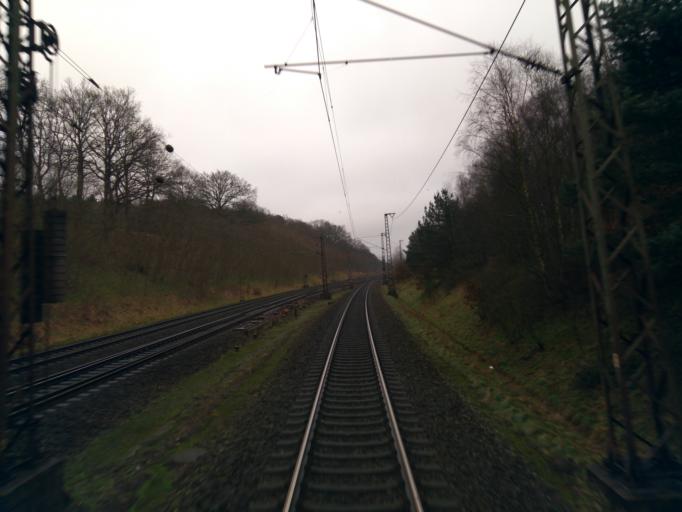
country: DE
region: Lower Saxony
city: Buchholz in der Nordheide
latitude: 53.3194
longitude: 9.8333
